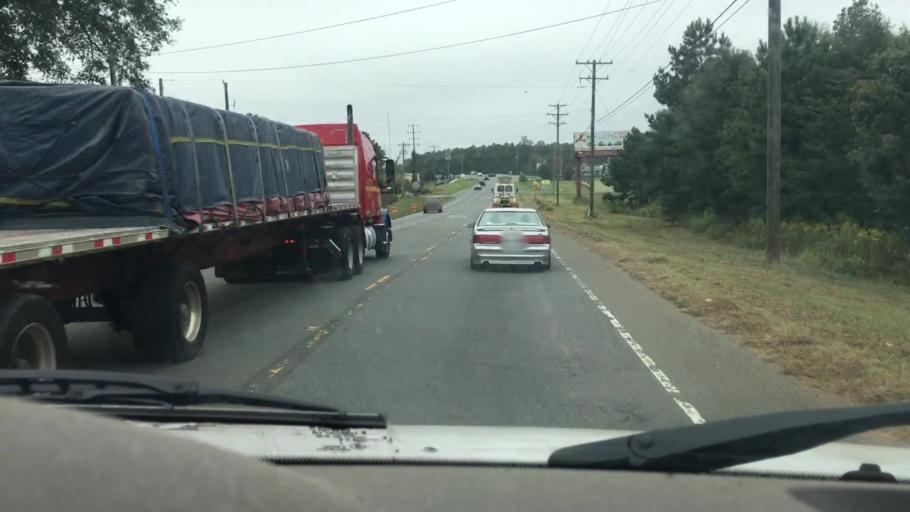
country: US
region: North Carolina
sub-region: Catawba County
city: Lake Norman of Catawba
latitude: 35.6031
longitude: -80.9005
